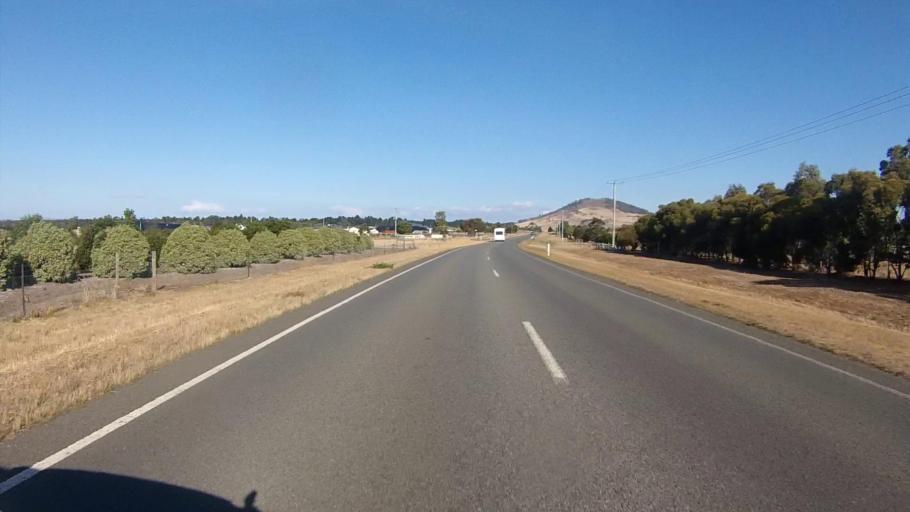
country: AU
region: Tasmania
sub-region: Clarence
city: Seven Mile Beach
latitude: -42.8477
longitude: 147.4817
